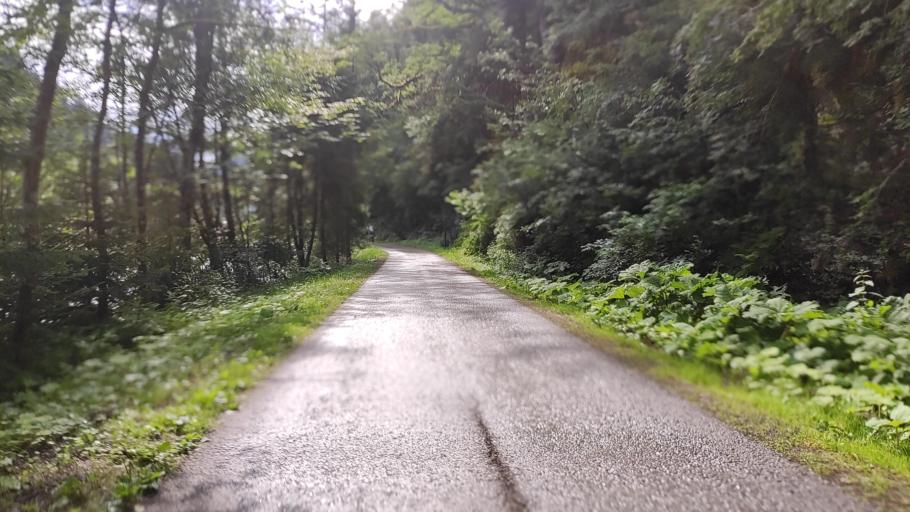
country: AT
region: Salzburg
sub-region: Politischer Bezirk Zell am See
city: Viehhofen
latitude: 47.3648
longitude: 12.7447
